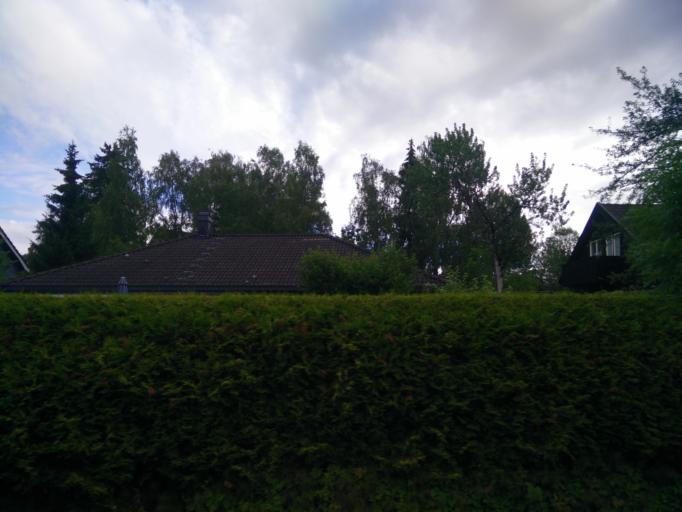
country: NO
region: Akershus
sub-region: Baerum
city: Lysaker
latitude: 59.9506
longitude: 10.6368
